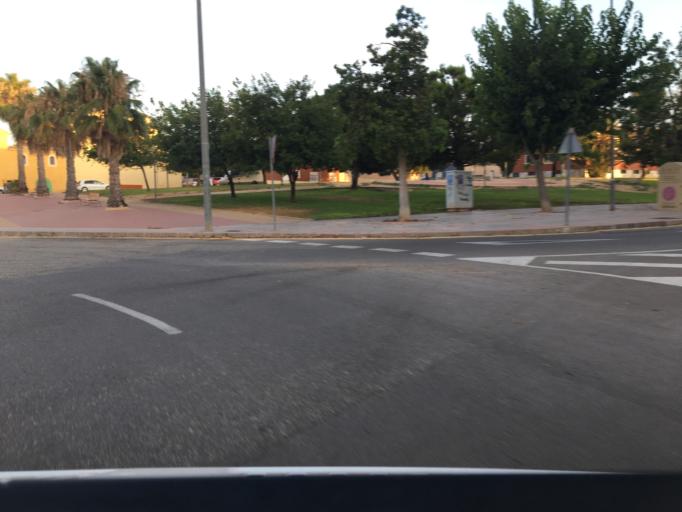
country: ES
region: Murcia
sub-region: Murcia
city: Cartagena
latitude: 37.6275
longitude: -0.9836
